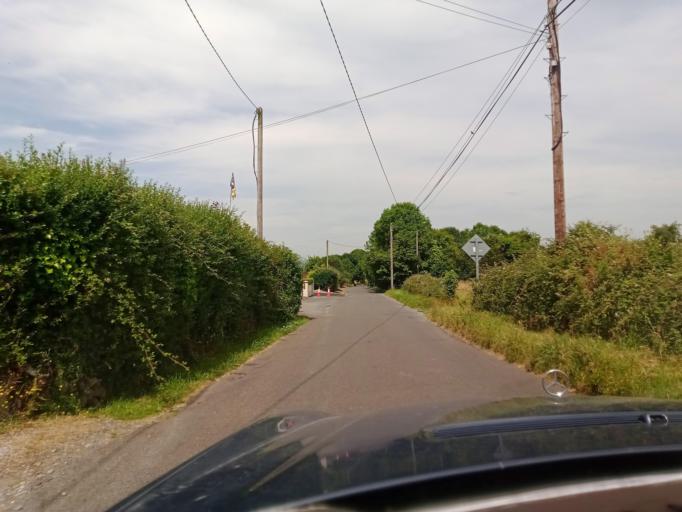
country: IE
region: Leinster
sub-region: Kilkenny
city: Mooncoin
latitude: 52.2722
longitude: -7.2165
